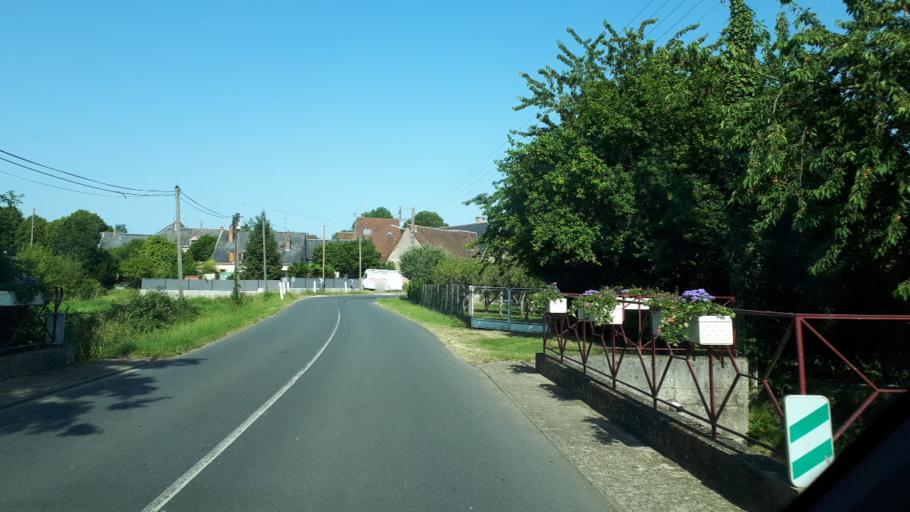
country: FR
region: Centre
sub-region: Departement du Loir-et-Cher
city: La Ville-aux-Clercs
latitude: 47.9584
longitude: 1.0770
